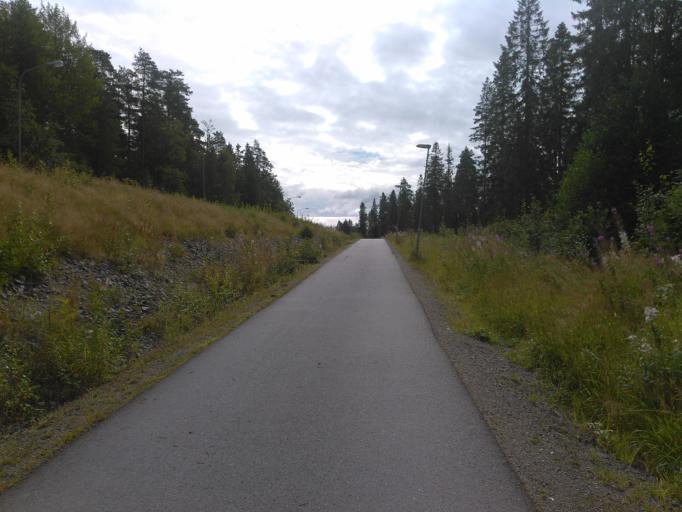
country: SE
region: Vaesterbotten
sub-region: Umea Kommun
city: Umea
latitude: 63.8244
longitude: 20.3127
